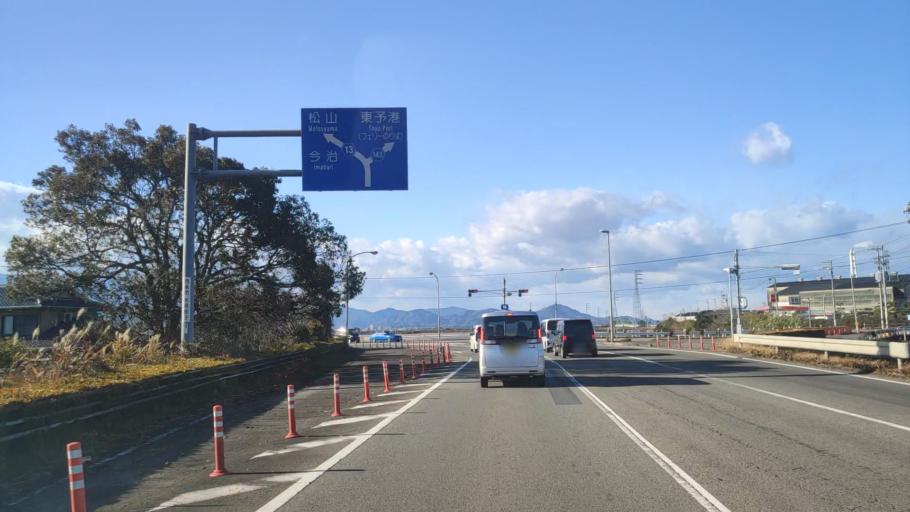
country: JP
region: Ehime
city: Saijo
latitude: 33.9186
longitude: 133.1252
